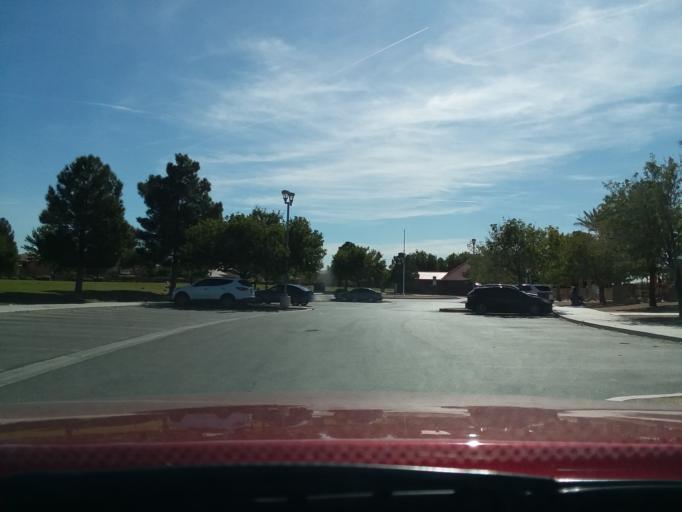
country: US
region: Nevada
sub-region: Clark County
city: North Las Vegas
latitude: 36.2883
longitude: -115.1764
